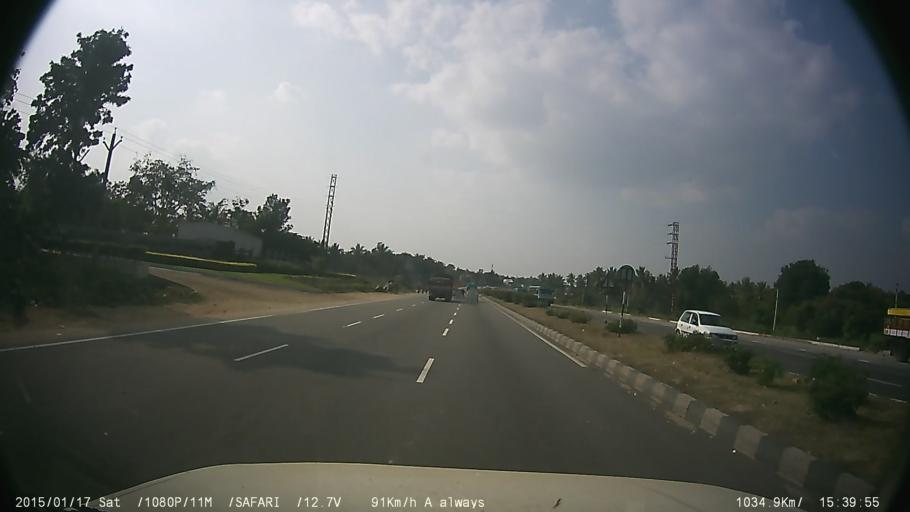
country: IN
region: Tamil Nadu
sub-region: Krishnagiri
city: Kelamangalam
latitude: 12.6720
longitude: 77.9729
